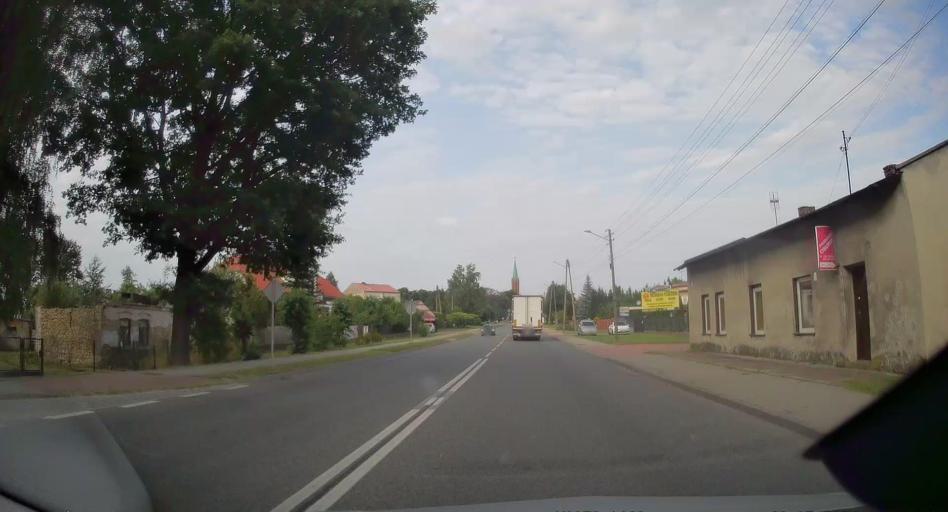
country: PL
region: Silesian Voivodeship
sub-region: Powiat czestochowski
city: Redziny
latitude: 50.8550
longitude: 19.2051
